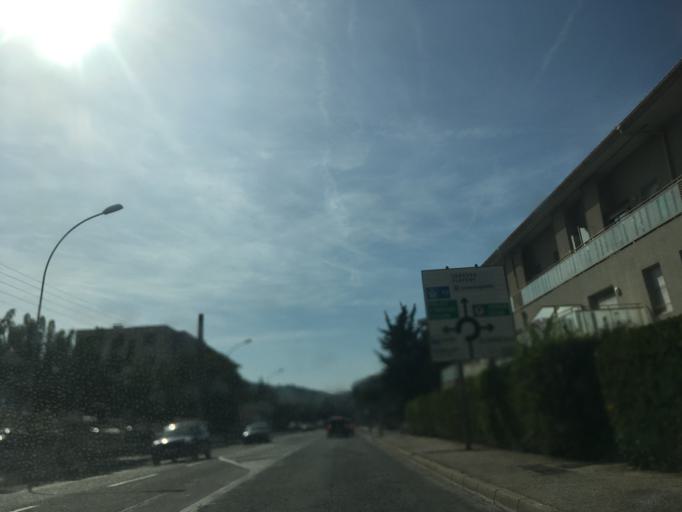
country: FR
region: Provence-Alpes-Cote d'Azur
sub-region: Departement du Var
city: Draguignan
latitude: 43.5309
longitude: 6.4726
